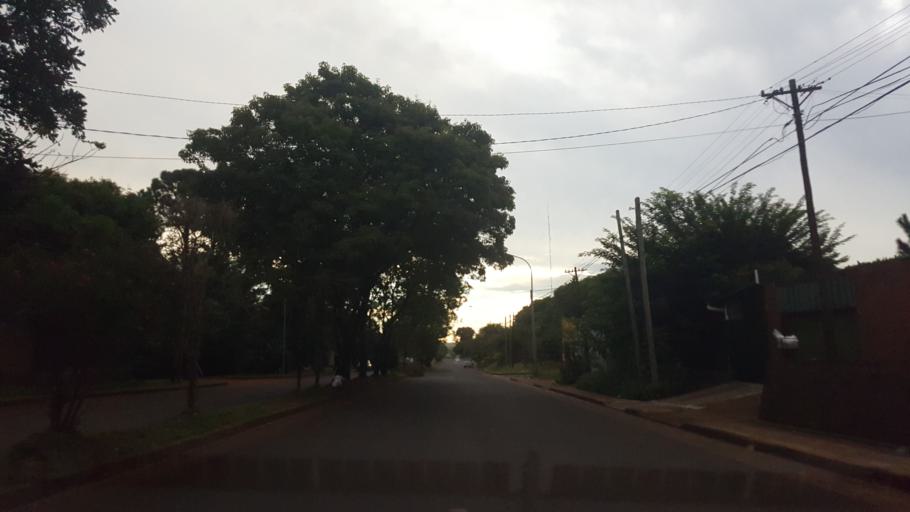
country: AR
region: Misiones
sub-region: Departamento de Capital
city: Posadas
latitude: -27.3929
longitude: -55.9143
